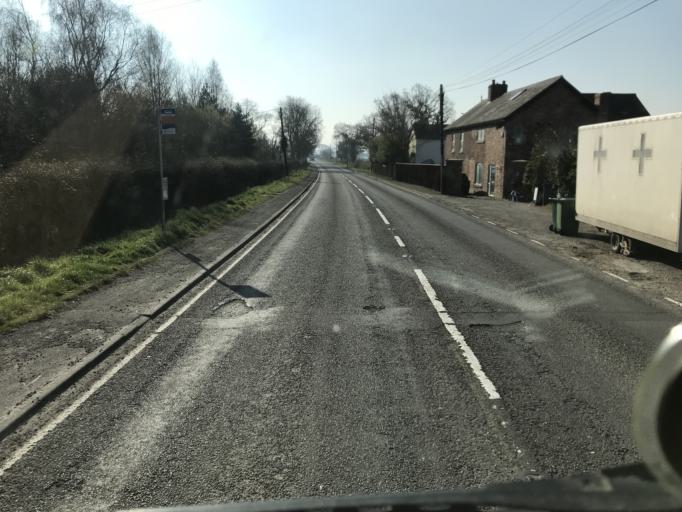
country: GB
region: England
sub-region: Cheshire West and Chester
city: Waverton
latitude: 53.1415
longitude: -2.8114
